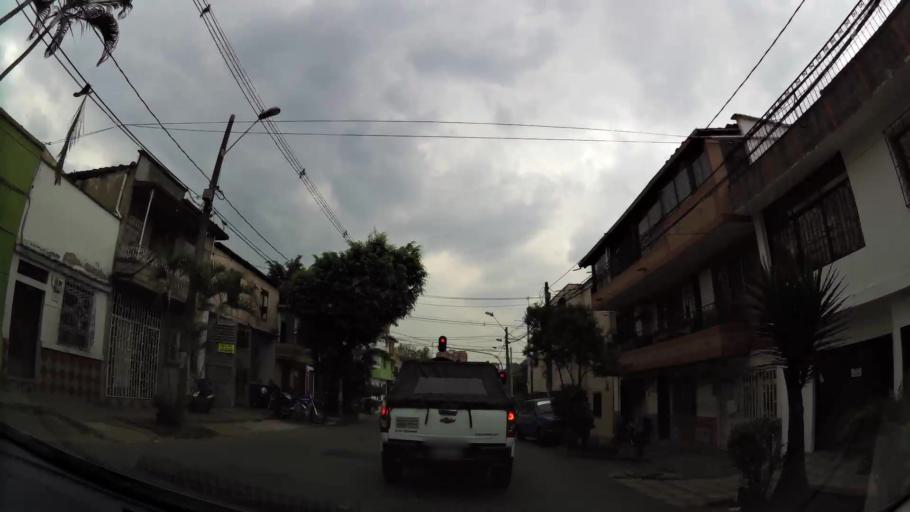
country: CO
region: Antioquia
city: Medellin
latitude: 6.2466
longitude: -75.5553
